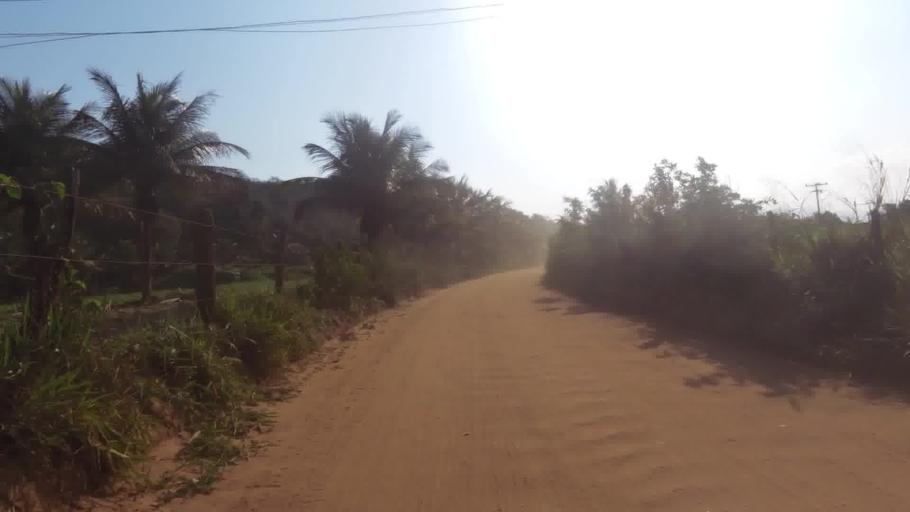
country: BR
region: Espirito Santo
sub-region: Piuma
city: Piuma
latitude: -20.8543
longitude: -40.7562
